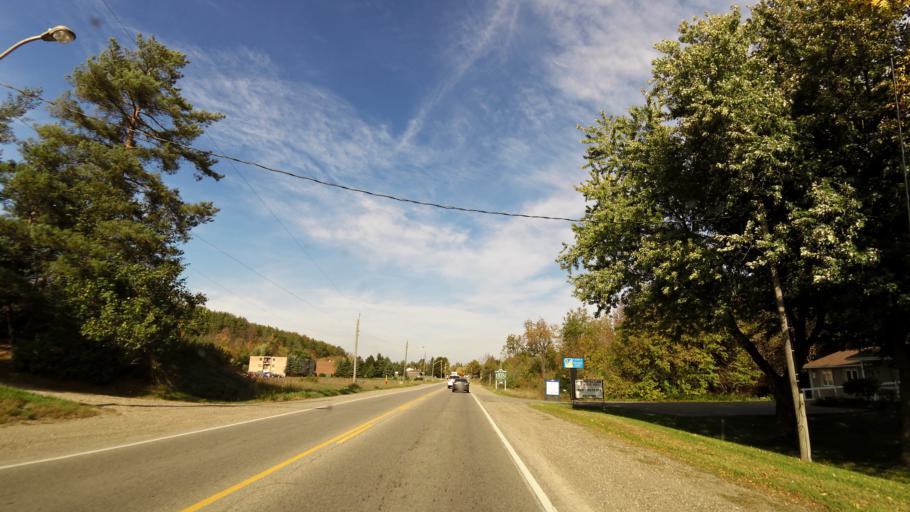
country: CA
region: Ontario
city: Orangeville
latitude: 43.7618
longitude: -80.0605
